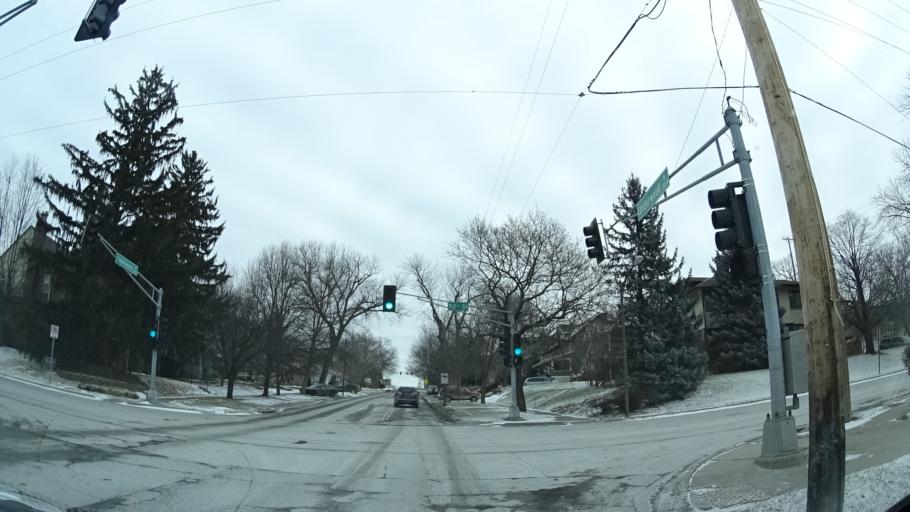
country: US
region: Nebraska
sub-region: Douglas County
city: Omaha
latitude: 41.2650
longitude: -95.9953
